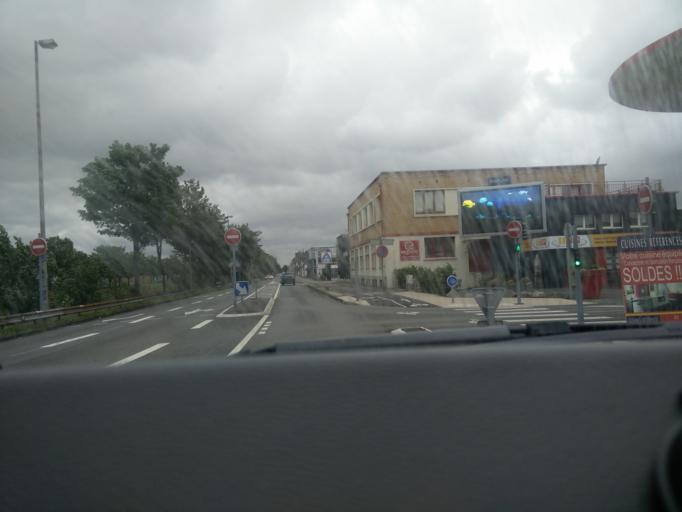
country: FR
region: Nord-Pas-de-Calais
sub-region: Departement du Nord
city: Dunkerque
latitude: 51.0234
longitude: 2.3742
